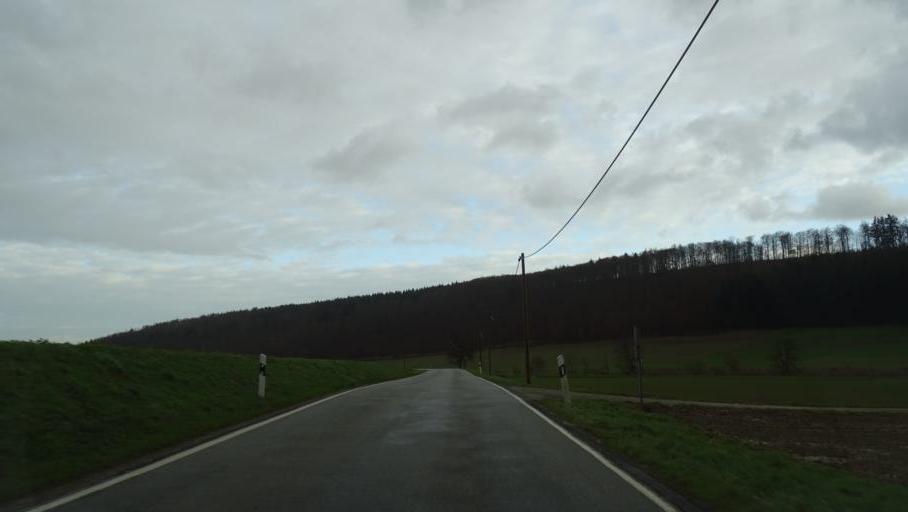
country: DE
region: Baden-Wuerttemberg
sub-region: Karlsruhe Region
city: Binau
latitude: 49.3836
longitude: 9.0419
